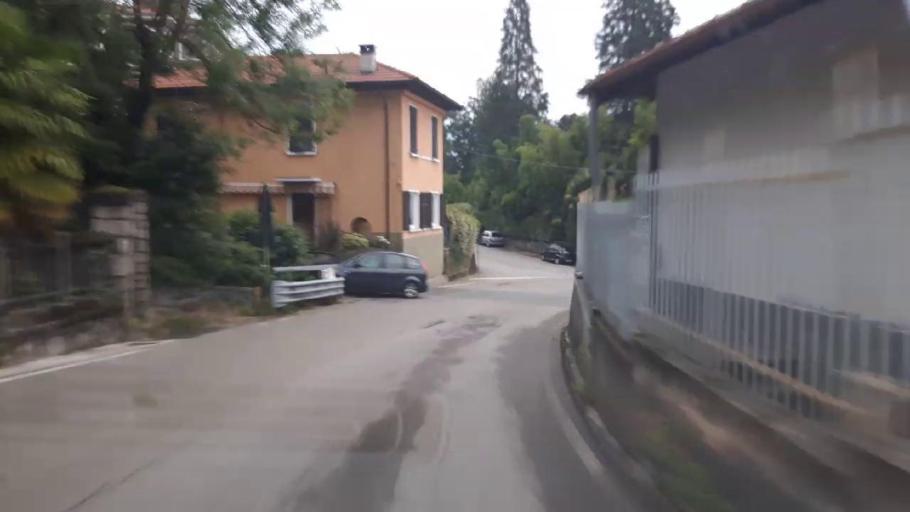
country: IT
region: Piedmont
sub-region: Provincia Verbano-Cusio-Ossola
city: Baveno
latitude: 45.9053
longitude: 8.4995
